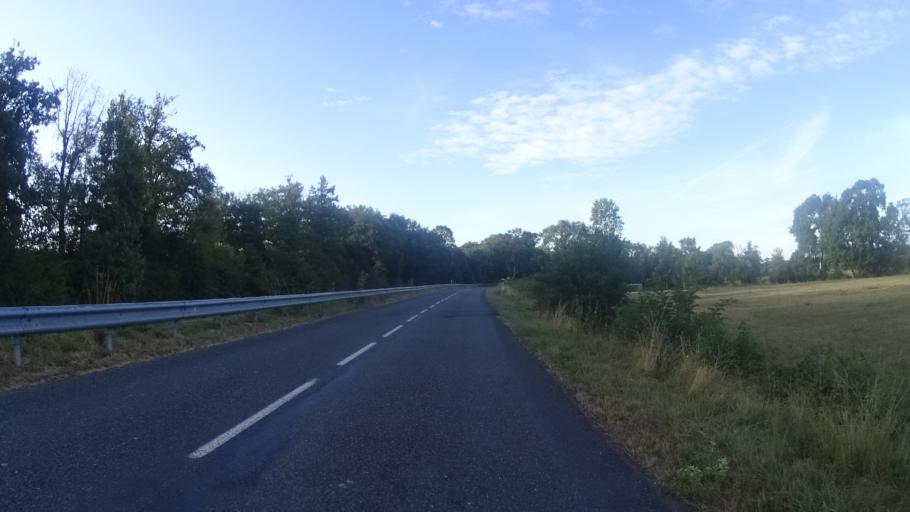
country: FR
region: Bourgogne
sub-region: Departement de Saone-et-Loire
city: Paray-le-Monial
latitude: 46.4546
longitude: 4.1579
